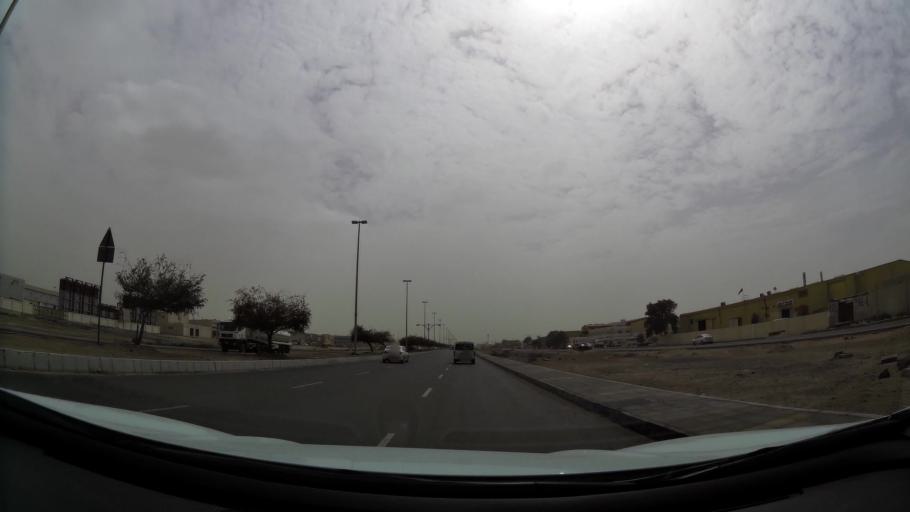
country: AE
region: Abu Dhabi
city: Abu Dhabi
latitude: 24.3523
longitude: 54.4725
